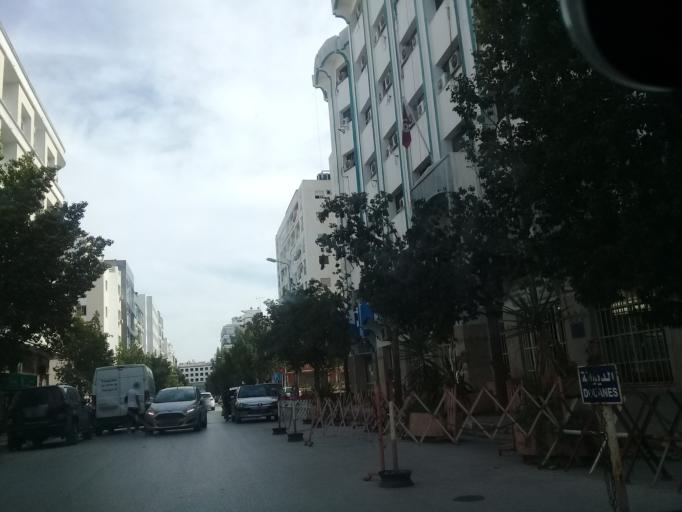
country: TN
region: Tunis
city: Tunis
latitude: 36.8160
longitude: 10.1809
